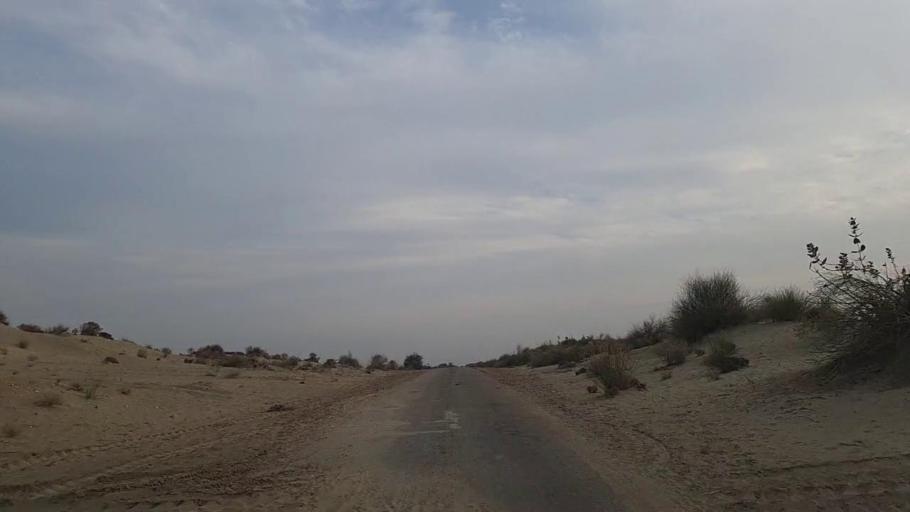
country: PK
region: Sindh
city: Jam Sahib
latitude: 26.4841
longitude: 68.5607
